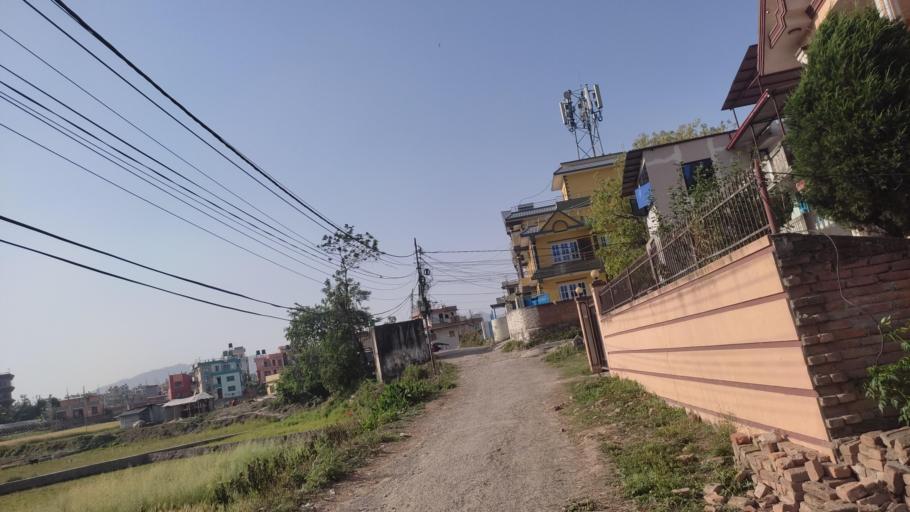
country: NP
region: Central Region
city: Kirtipur
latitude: 27.6611
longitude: 85.2782
